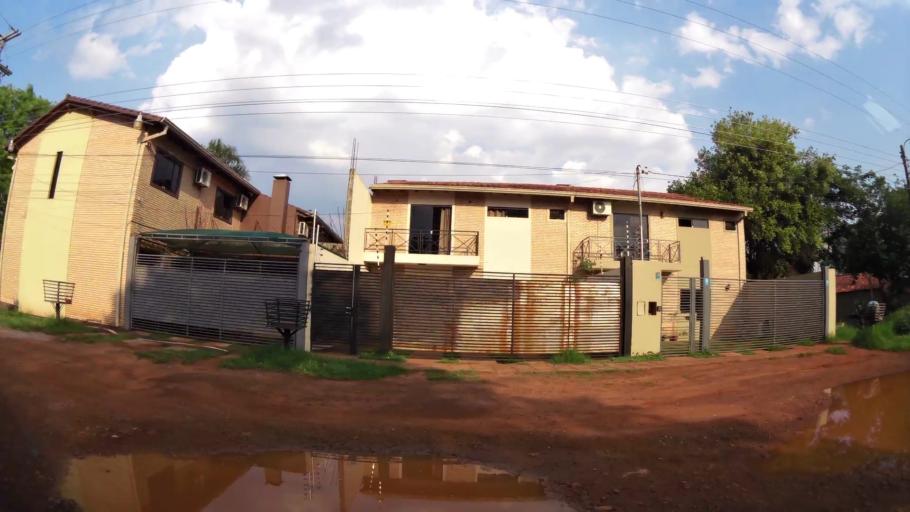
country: PY
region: Alto Parana
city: Presidente Franco
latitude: -25.5204
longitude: -54.6264
